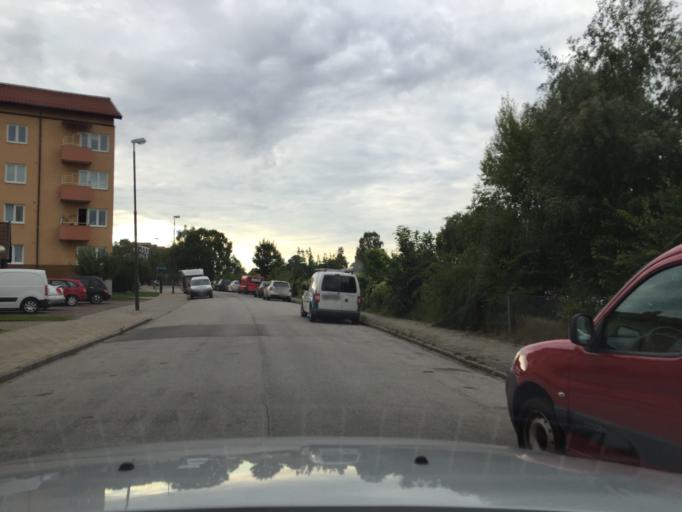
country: SE
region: Skane
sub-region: Malmo
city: Malmoe
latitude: 55.6047
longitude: 13.0332
